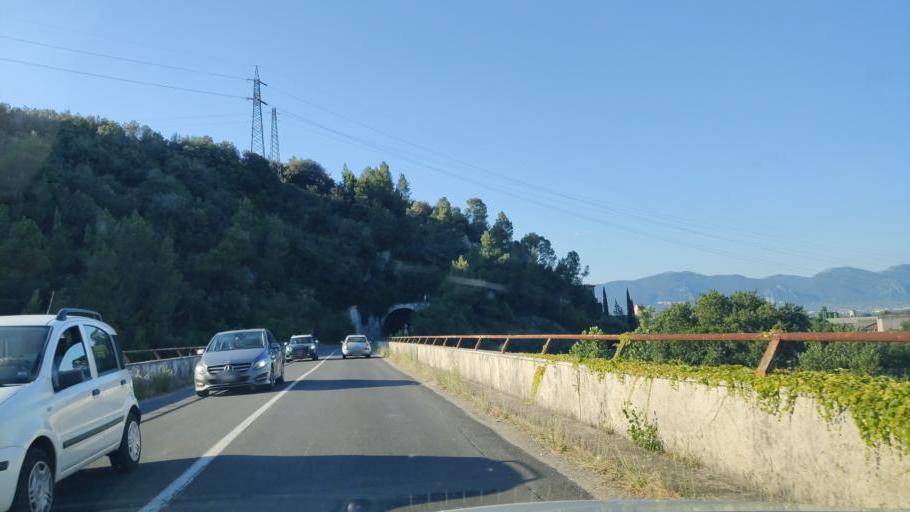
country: IT
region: Umbria
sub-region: Provincia di Terni
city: Narni Scalo
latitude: 42.5251
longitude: 12.5130
